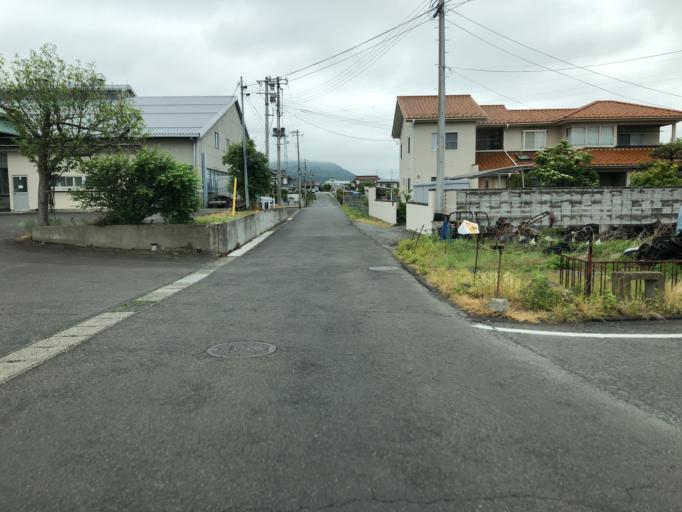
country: JP
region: Fukushima
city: Fukushima-shi
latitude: 37.7714
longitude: 140.3930
